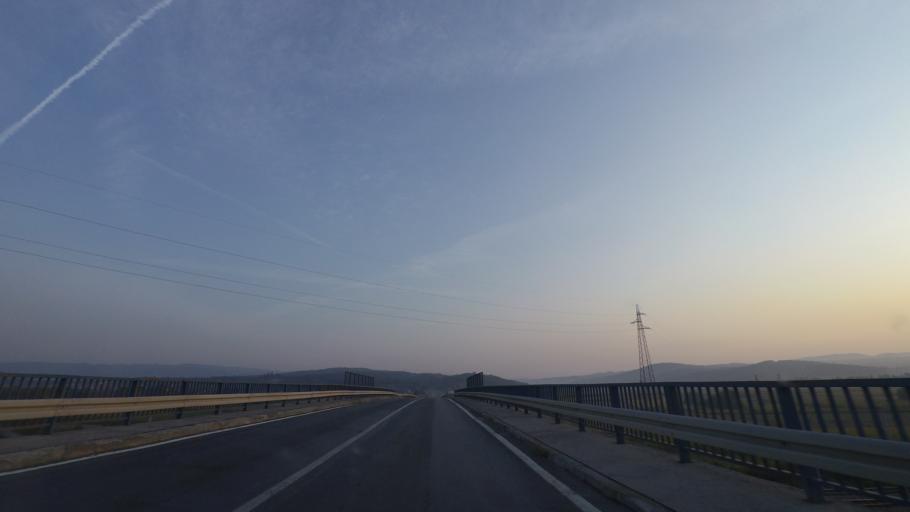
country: HR
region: Brodsko-Posavska
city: Nova Gradiska
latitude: 45.2467
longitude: 17.4082
